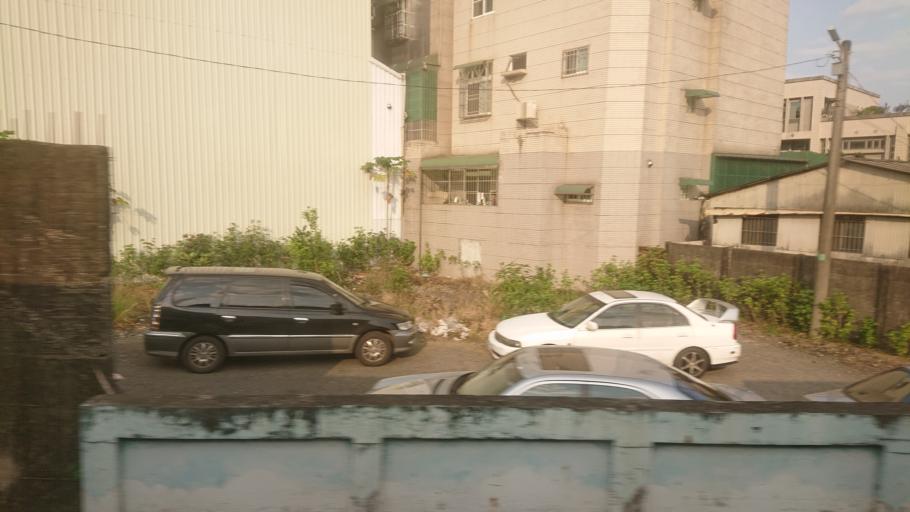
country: TW
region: Taiwan
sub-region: Chiayi
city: Jiayi Shi
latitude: 23.4886
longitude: 120.4492
